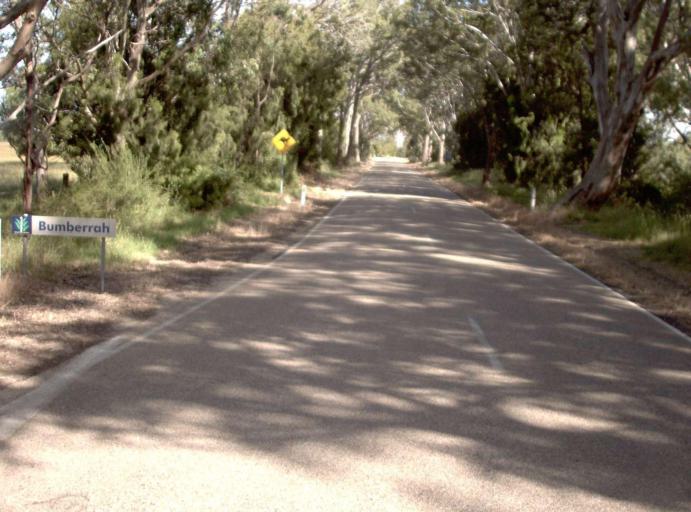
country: AU
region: Victoria
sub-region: East Gippsland
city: Lakes Entrance
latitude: -37.7998
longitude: 147.8345
